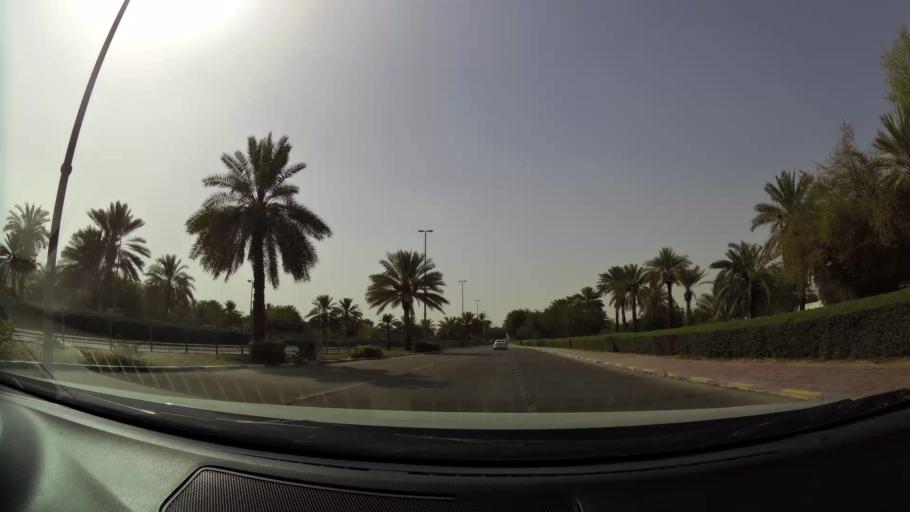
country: AE
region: Abu Dhabi
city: Al Ain
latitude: 24.2334
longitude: 55.6918
